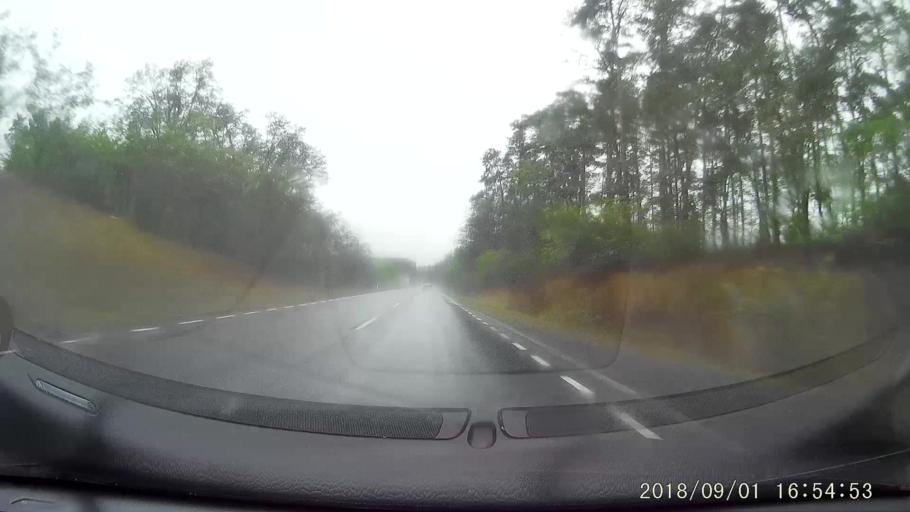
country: PL
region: Lubusz
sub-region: Zielona Gora
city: Zielona Gora
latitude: 51.9531
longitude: 15.4478
